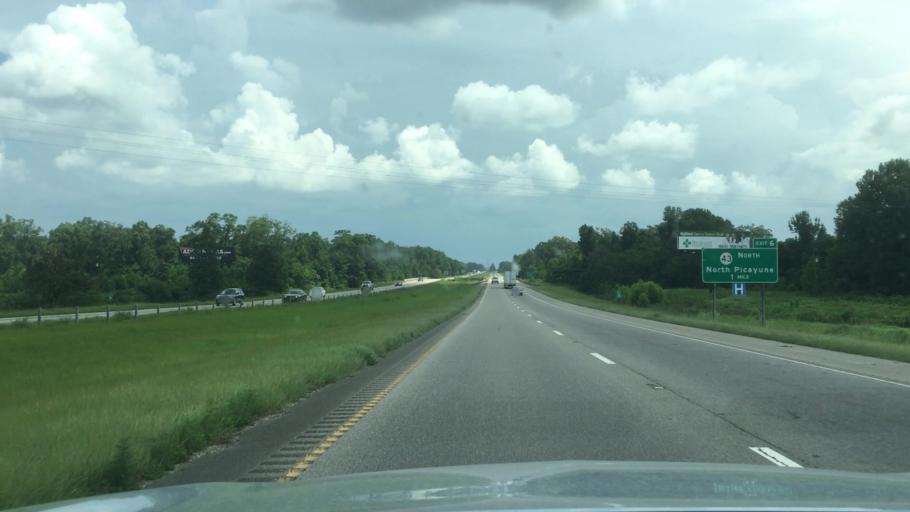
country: US
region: Mississippi
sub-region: Pearl River County
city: Picayune
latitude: 30.5252
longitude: -89.6595
